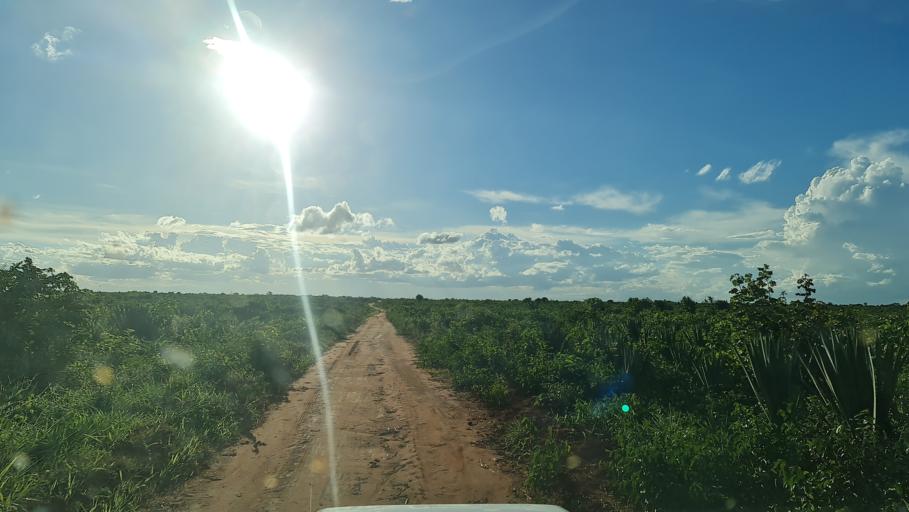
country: MZ
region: Nampula
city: Ilha de Mocambique
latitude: -14.9521
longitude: 40.1783
